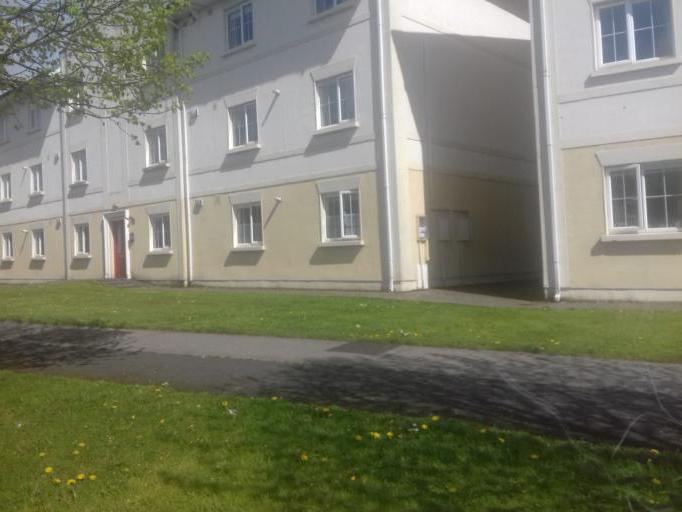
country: IE
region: Leinster
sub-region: Laois
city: Portlaoise
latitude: 53.0397
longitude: -7.2973
